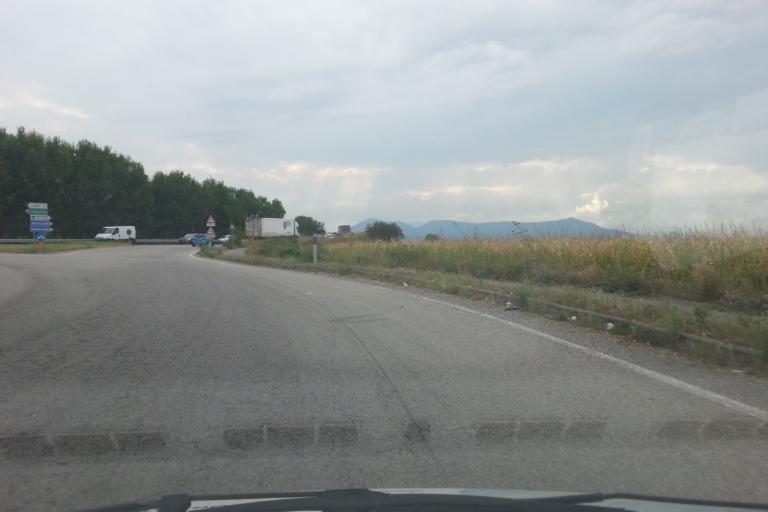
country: IT
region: Piedmont
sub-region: Provincia di Torino
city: Tetti Neirotti
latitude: 45.0426
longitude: 7.5611
